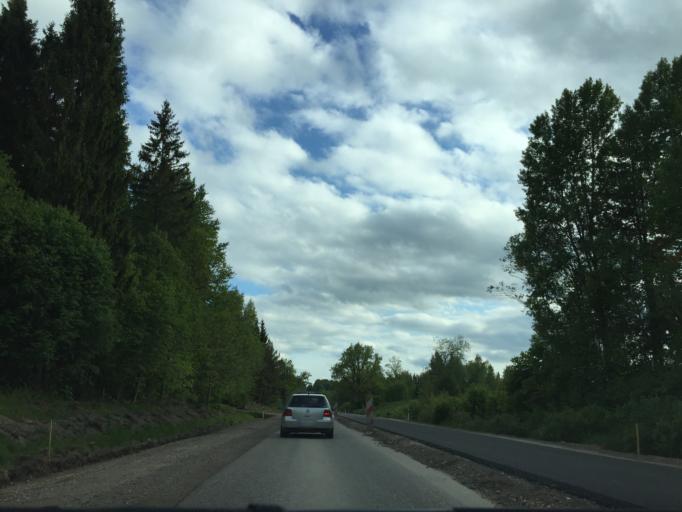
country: LV
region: Amatas Novads
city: Drabesi
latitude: 57.2524
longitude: 25.2623
